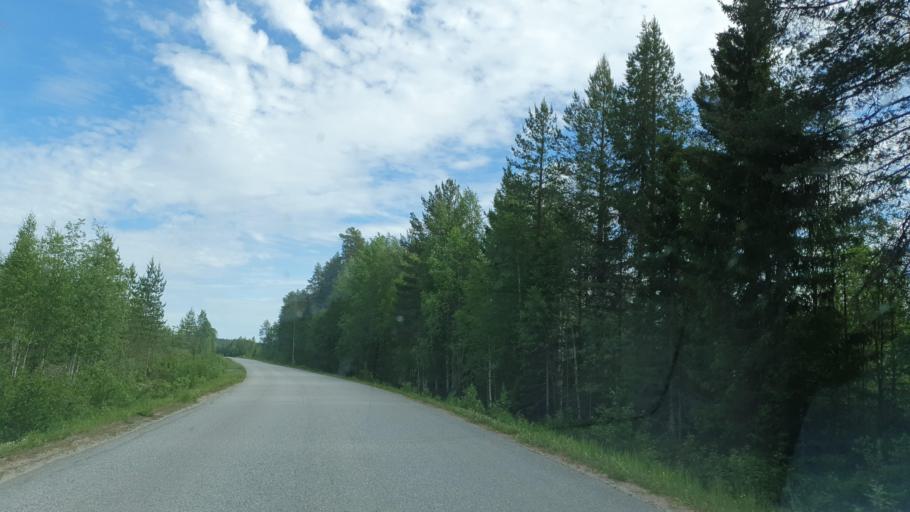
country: FI
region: Kainuu
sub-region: Kehys-Kainuu
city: Suomussalmi
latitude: 64.5562
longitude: 29.1574
